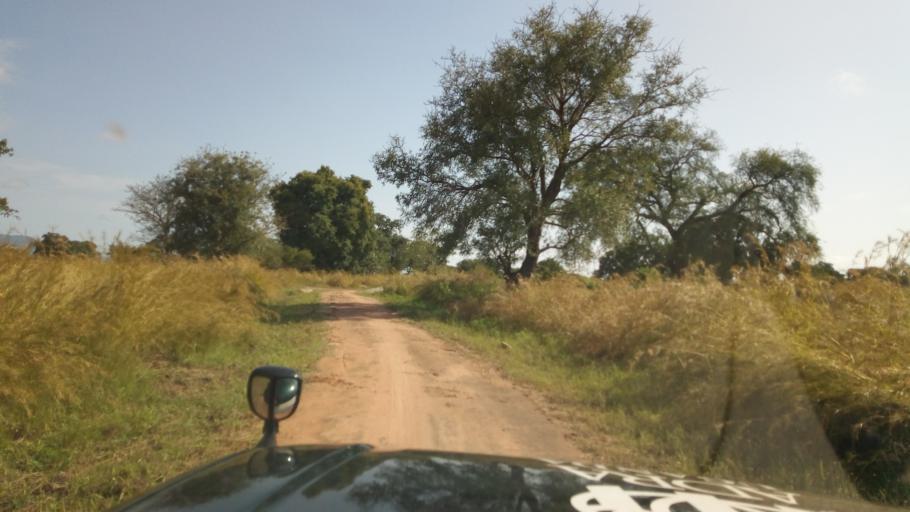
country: UG
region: Northern Region
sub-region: Adjumani District
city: Adjumani
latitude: 3.4566
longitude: 31.8889
